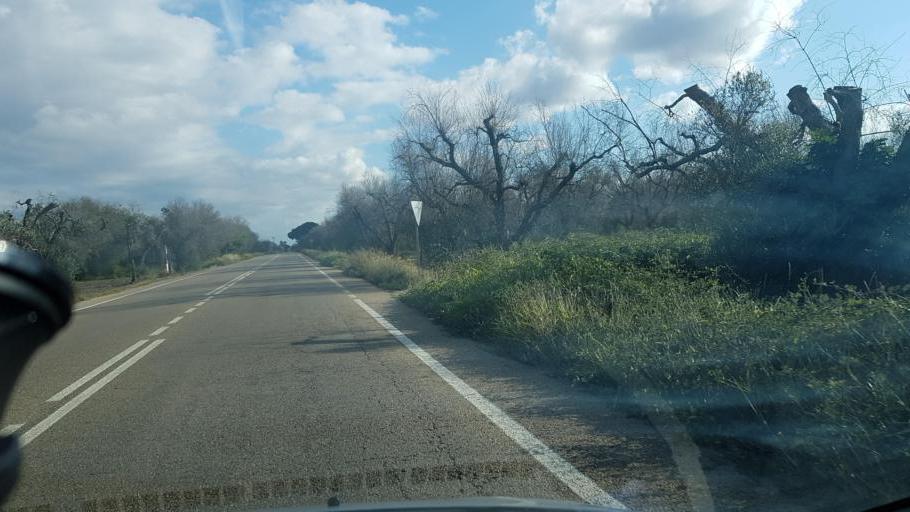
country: IT
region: Apulia
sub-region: Provincia di Lecce
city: Squinzano
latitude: 40.4553
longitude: 18.0248
